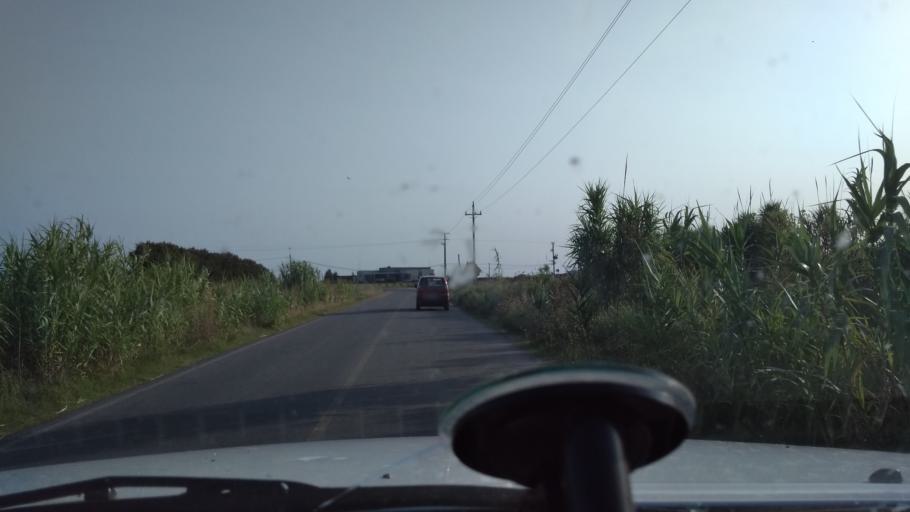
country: UY
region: Canelones
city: Colonia Nicolich
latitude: -34.7818
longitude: -56.0195
